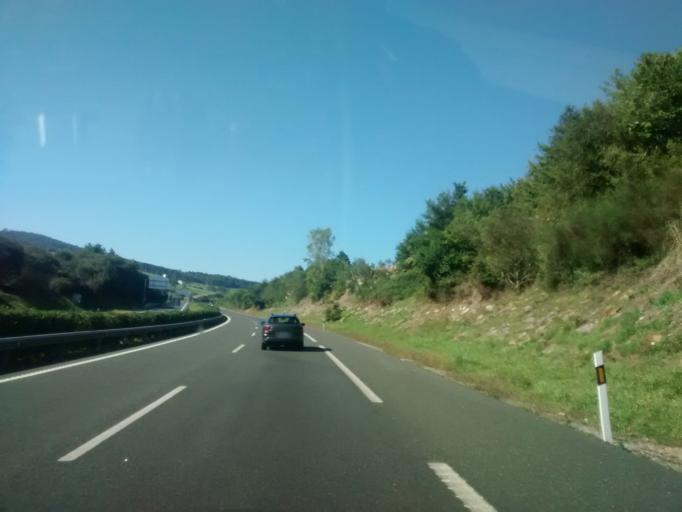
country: ES
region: Cantabria
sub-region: Provincia de Cantabria
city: Reocin
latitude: 43.3541
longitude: -4.1035
